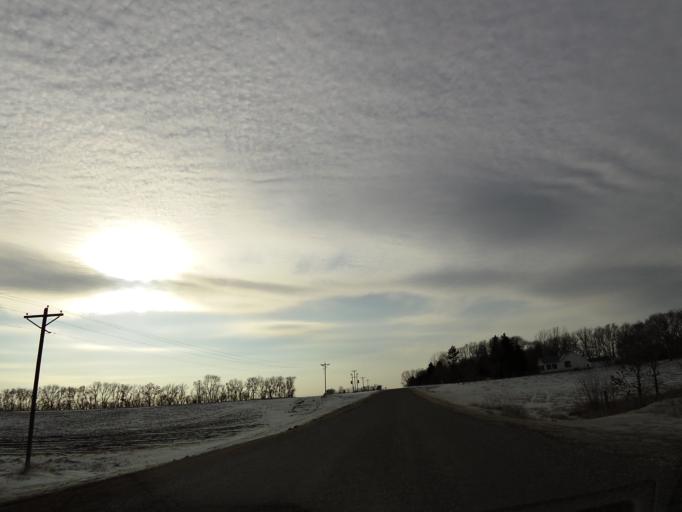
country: US
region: North Dakota
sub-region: Walsh County
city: Grafton
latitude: 48.4268
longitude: -97.3125
